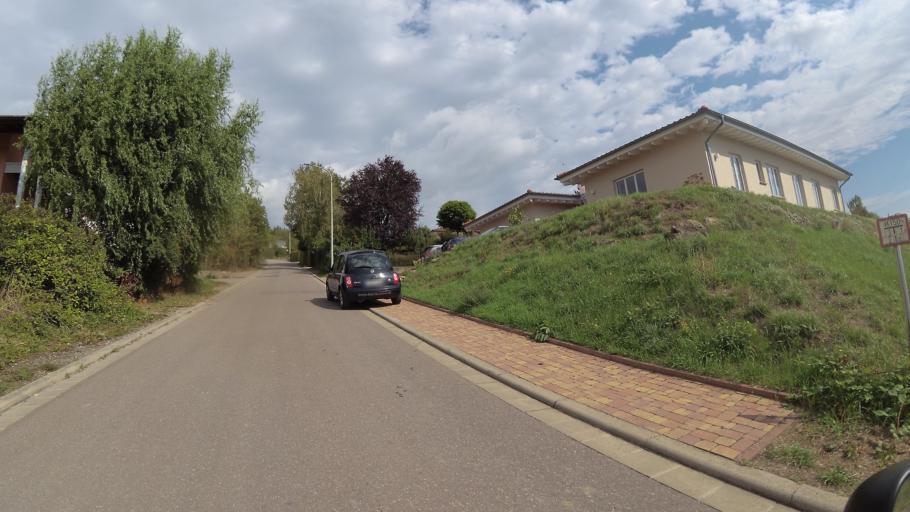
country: DE
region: Saarland
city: Gersheim
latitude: 49.1408
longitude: 7.1805
